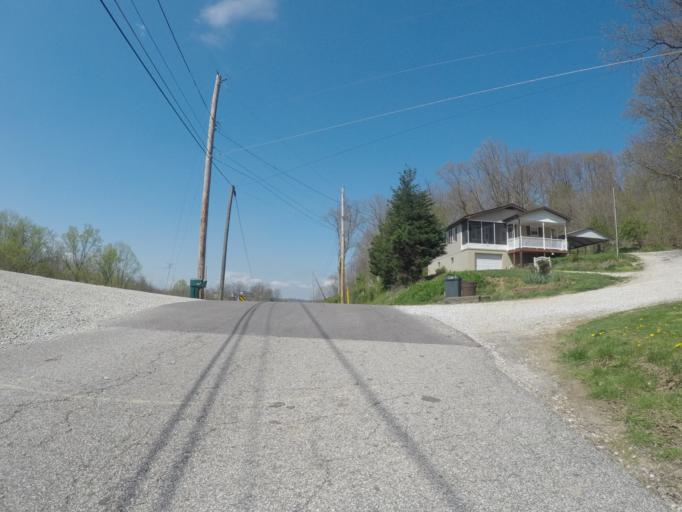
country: US
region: Ohio
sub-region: Lawrence County
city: Burlington
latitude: 38.3823
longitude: -82.5326
